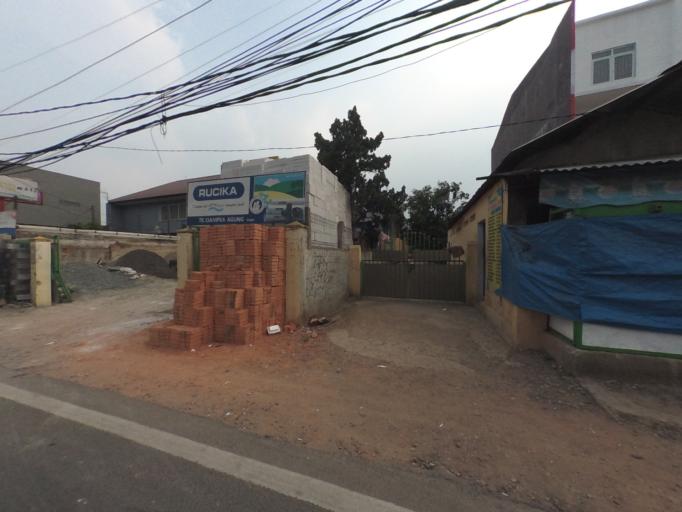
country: ID
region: West Java
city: Ciampea
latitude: -6.5548
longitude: 106.6986
